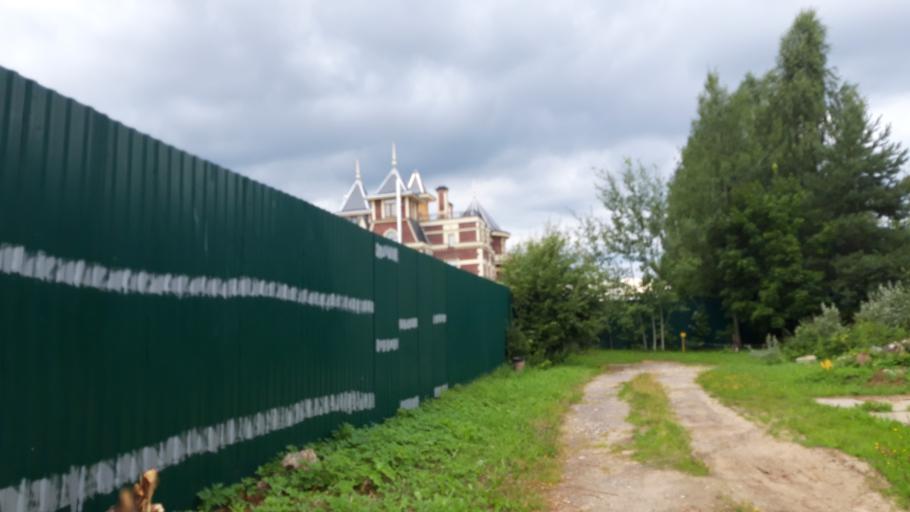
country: RU
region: Tverskaya
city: Konakovo
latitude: 56.6770
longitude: 36.7212
